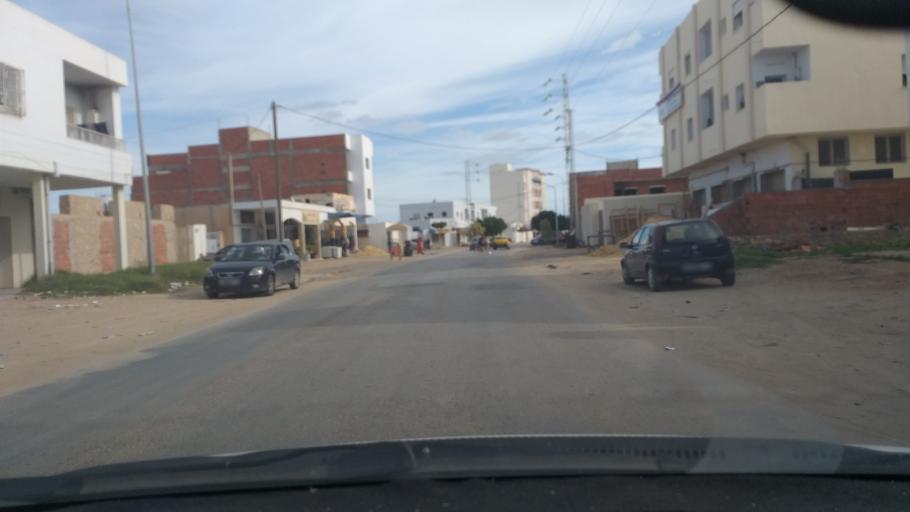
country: TN
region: Safaqis
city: Al Qarmadah
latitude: 34.7982
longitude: 10.7978
